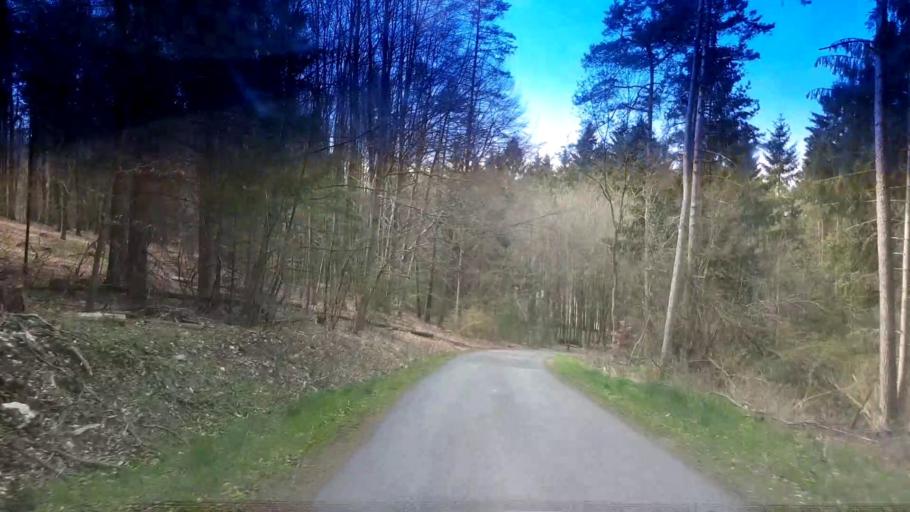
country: DE
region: Bavaria
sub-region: Upper Franconia
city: Poxdorf
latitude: 49.8834
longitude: 11.0869
